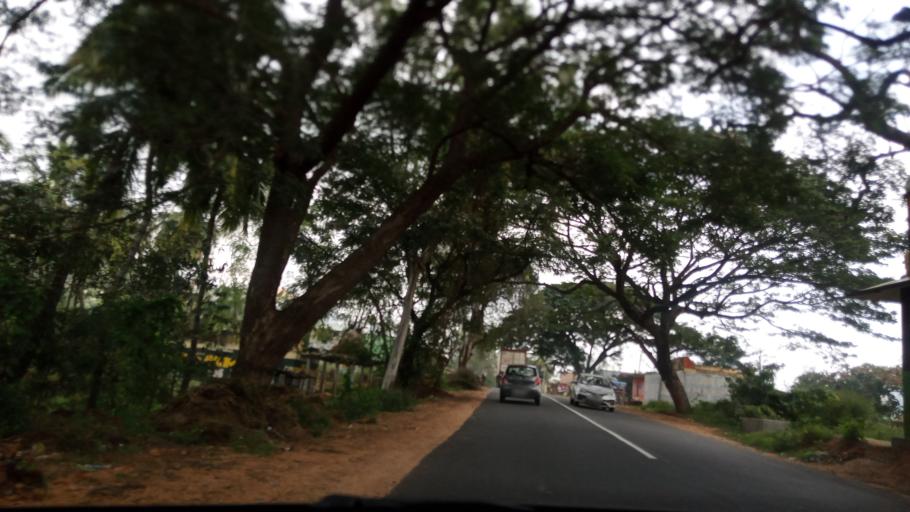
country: IN
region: Andhra Pradesh
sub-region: Chittoor
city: Madanapalle
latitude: 13.6365
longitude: 78.5869
